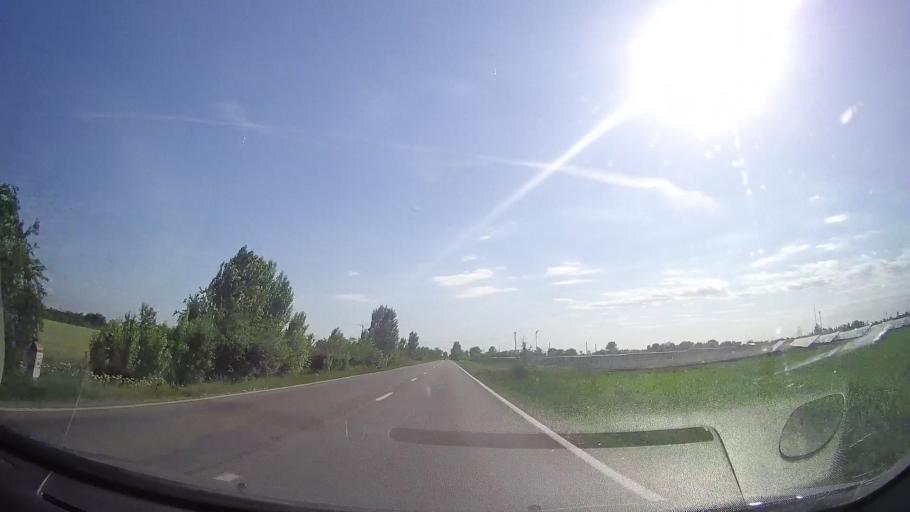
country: RO
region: Prahova
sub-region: Comuna Berceni
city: Corlatesti
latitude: 44.9049
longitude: 26.0717
